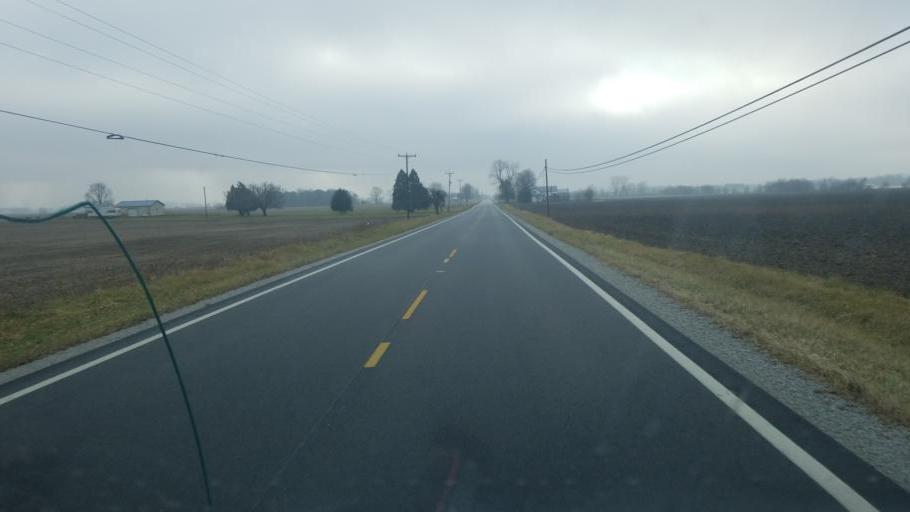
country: US
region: Ohio
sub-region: Hardin County
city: Kenton
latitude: 40.6780
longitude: -83.5196
